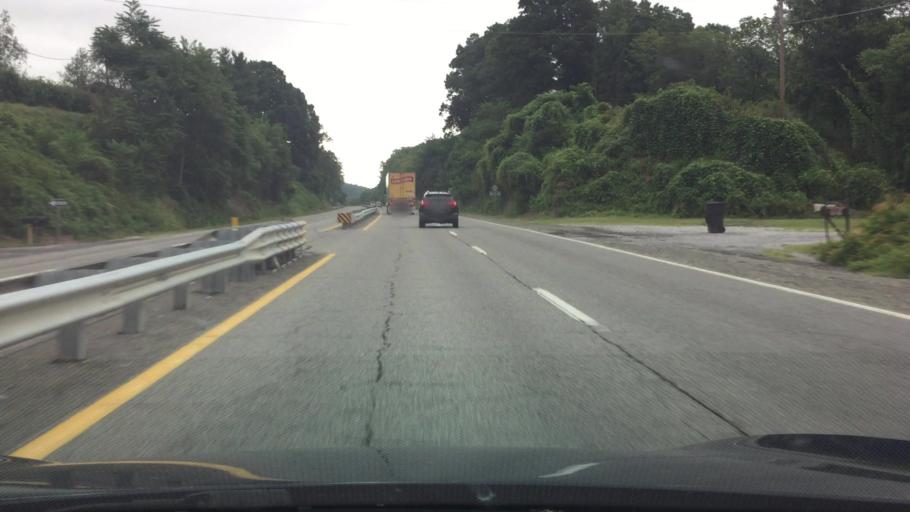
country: US
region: Virginia
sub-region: Montgomery County
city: Shawsville
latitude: 37.2369
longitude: -80.1871
